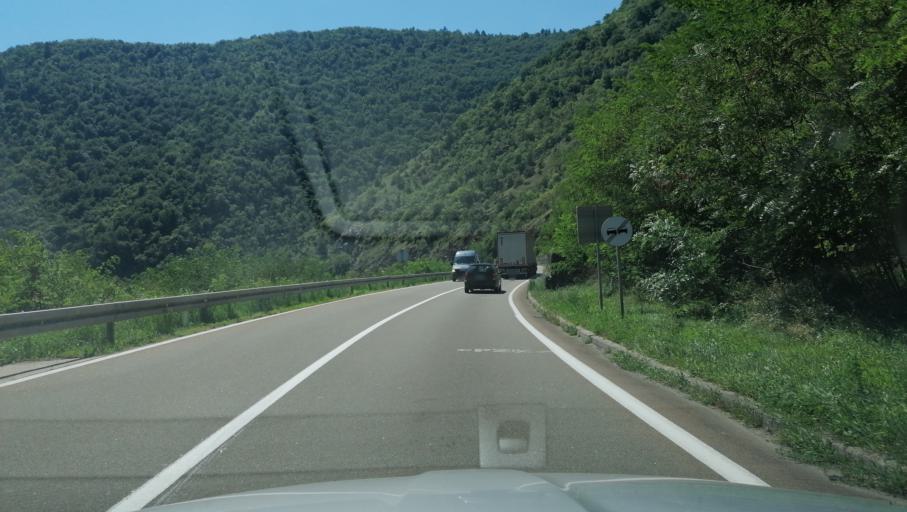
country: RS
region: Central Serbia
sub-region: Raski Okrug
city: Kraljevo
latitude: 43.5543
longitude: 20.6097
